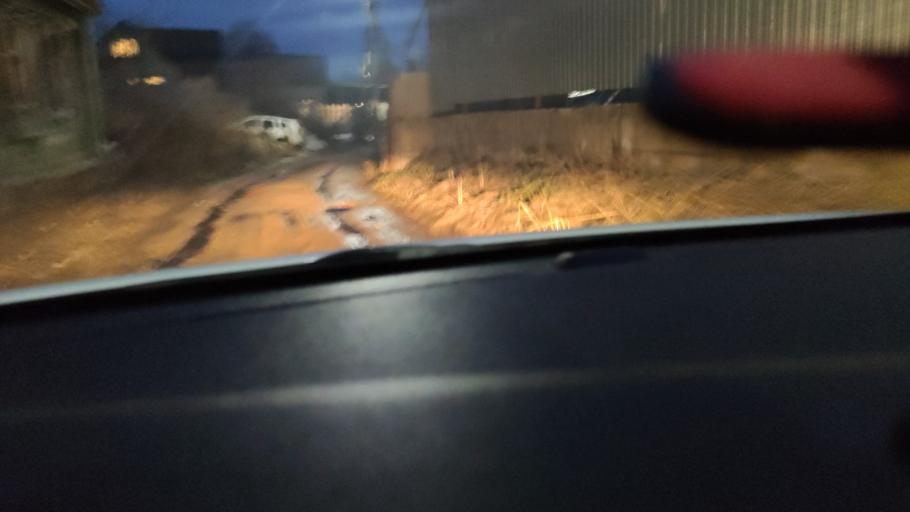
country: RU
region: Tatarstan
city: Staroye Arakchino
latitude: 55.8715
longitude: 49.0393
